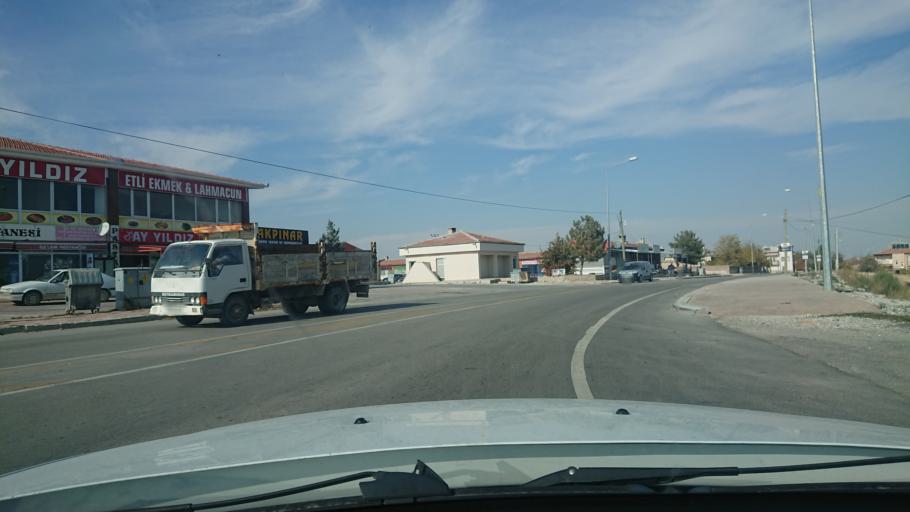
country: TR
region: Aksaray
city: Sultanhani
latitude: 38.2479
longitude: 33.4491
